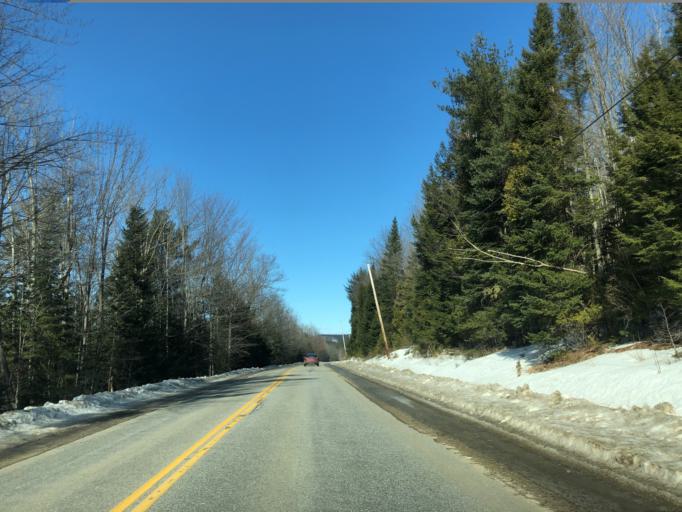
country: US
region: Maine
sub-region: Oxford County
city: Buckfield
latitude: 44.2531
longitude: -70.3375
